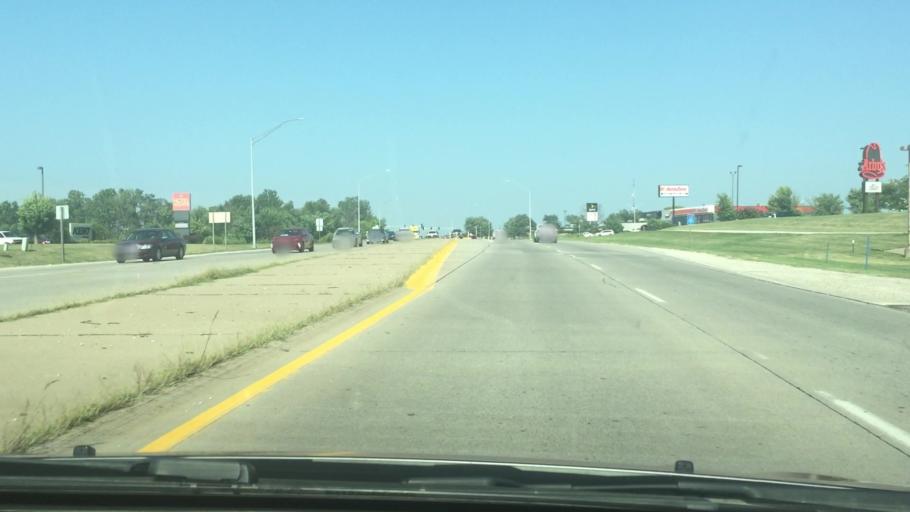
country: US
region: Iowa
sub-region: Muscatine County
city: Muscatine
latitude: 41.4541
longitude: -91.0285
